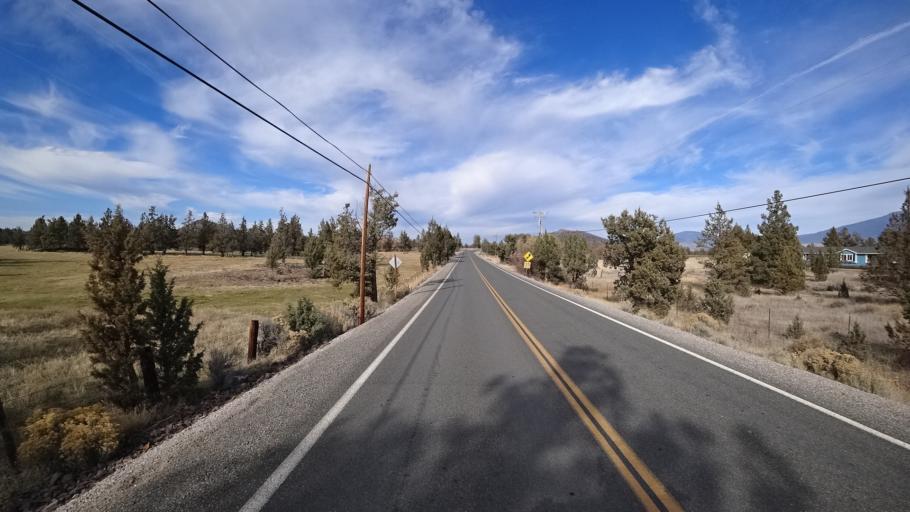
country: US
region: California
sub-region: Siskiyou County
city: Montague
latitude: 41.6395
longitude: -122.3995
